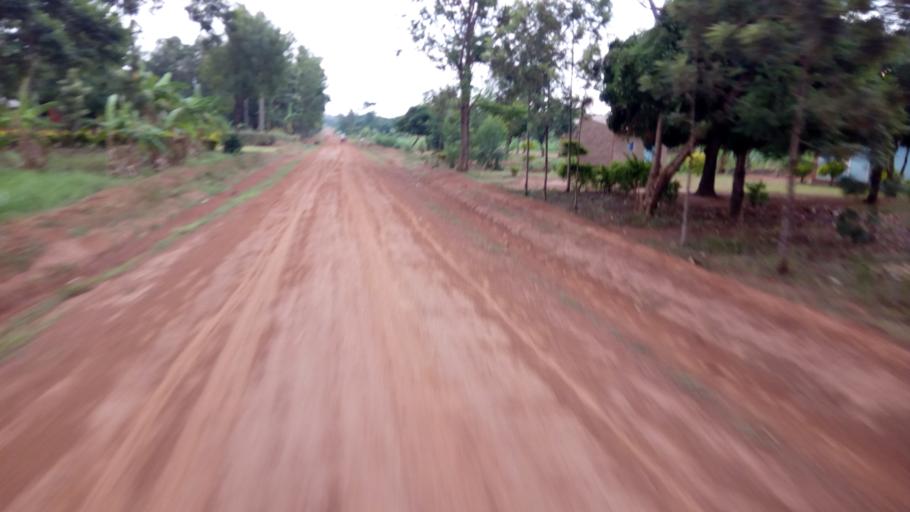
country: UG
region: Eastern Region
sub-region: Mbale District
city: Mbale
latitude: 1.1206
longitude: 34.1006
